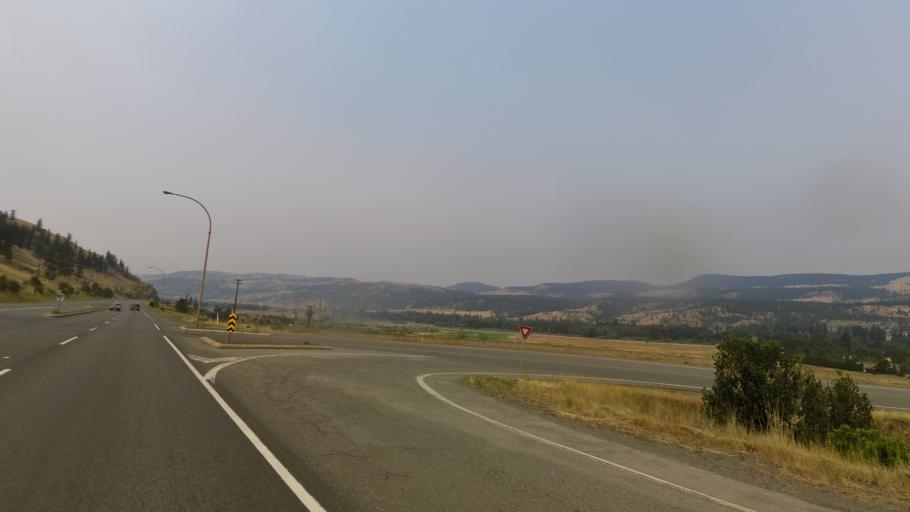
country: CA
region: British Columbia
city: Kamloops
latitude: 50.8329
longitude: -120.2789
